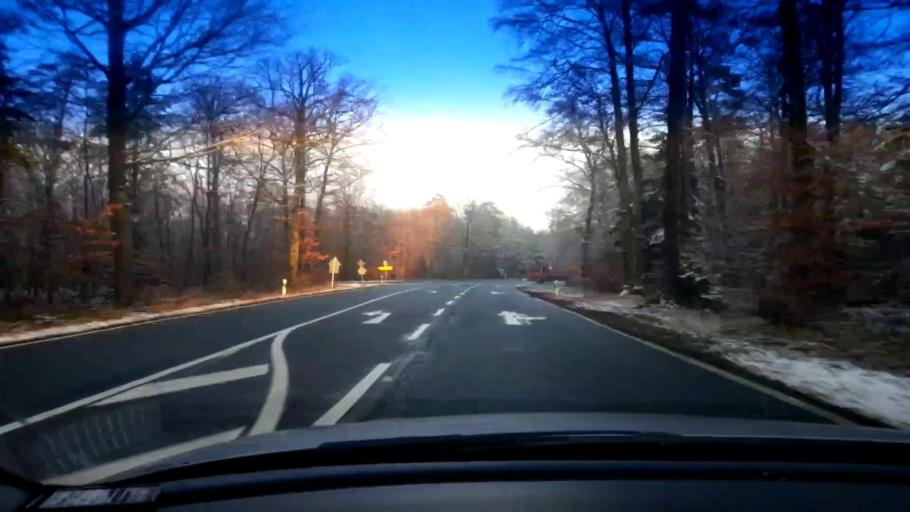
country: DE
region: Bavaria
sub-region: Regierungsbezirk Mittelfranken
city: Adelsdorf
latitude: 49.7530
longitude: 10.8656
